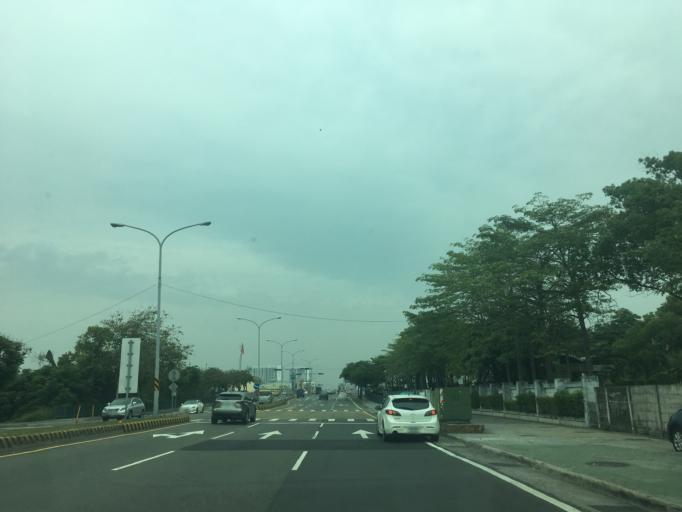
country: TW
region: Taiwan
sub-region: Taichung City
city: Taichung
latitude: 24.0765
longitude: 120.6997
